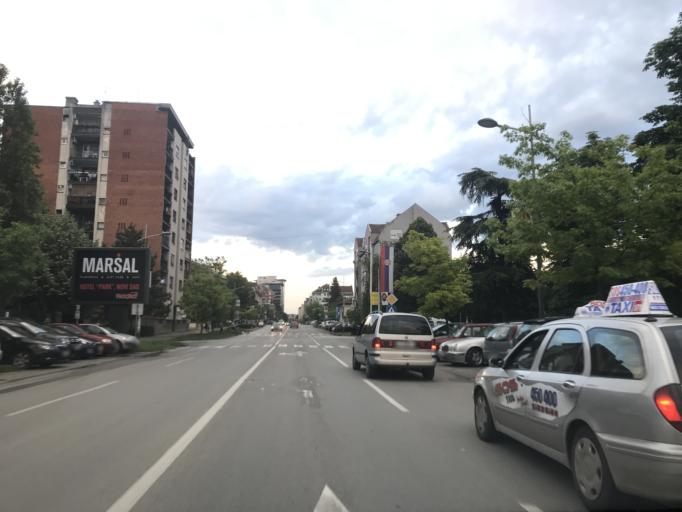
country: RS
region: Autonomna Pokrajina Vojvodina
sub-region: Juznobacki Okrug
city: Novi Sad
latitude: 45.2543
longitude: 19.8263
